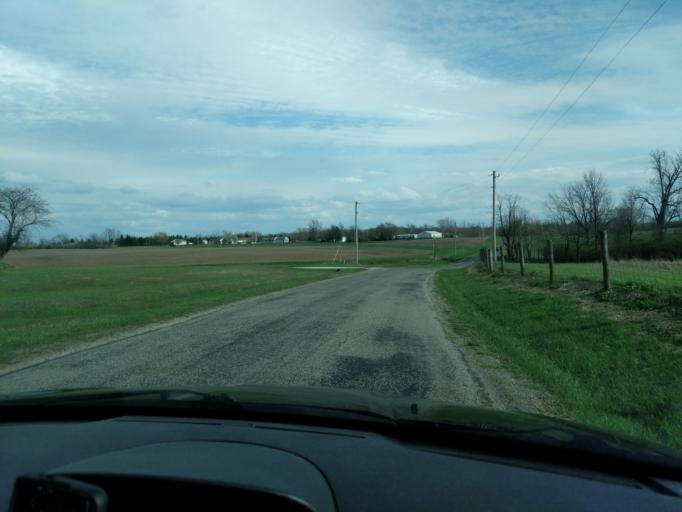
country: US
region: Ohio
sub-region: Champaign County
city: North Lewisburg
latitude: 40.1936
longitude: -83.6520
